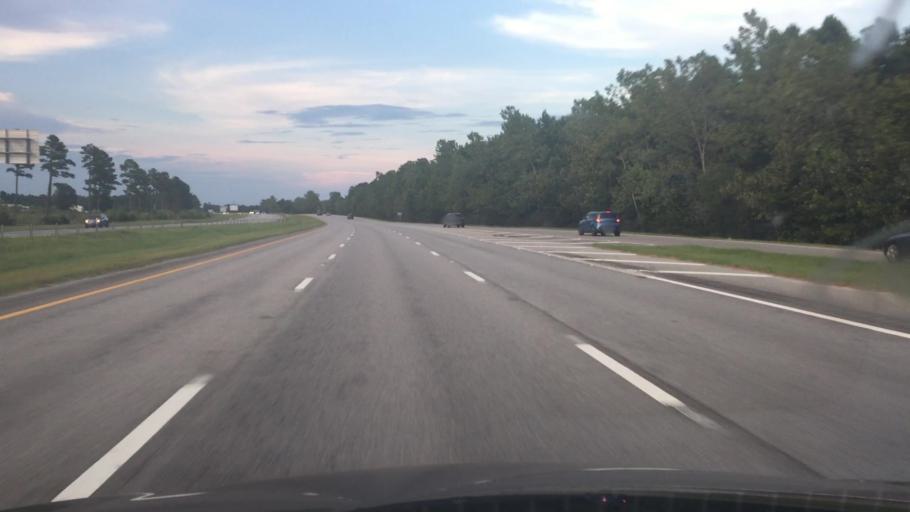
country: US
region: South Carolina
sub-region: Horry County
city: Myrtle Beach
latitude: 33.7553
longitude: -78.8489
